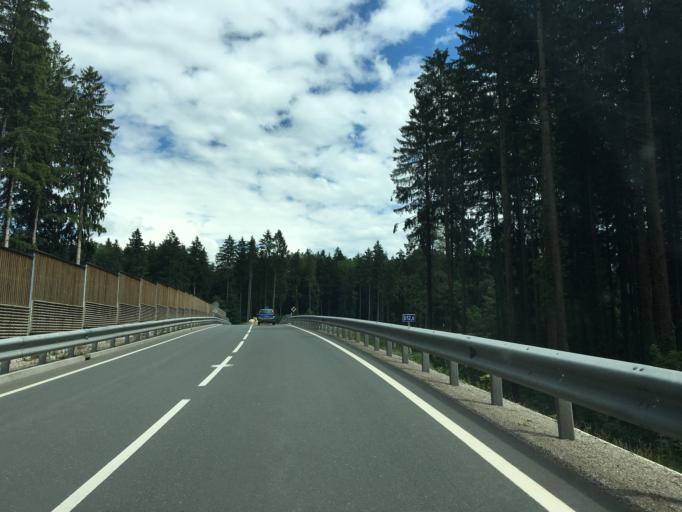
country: AT
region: Salzburg
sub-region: Politischer Bezirk Hallein
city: Adnet
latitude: 47.6630
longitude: 13.1220
